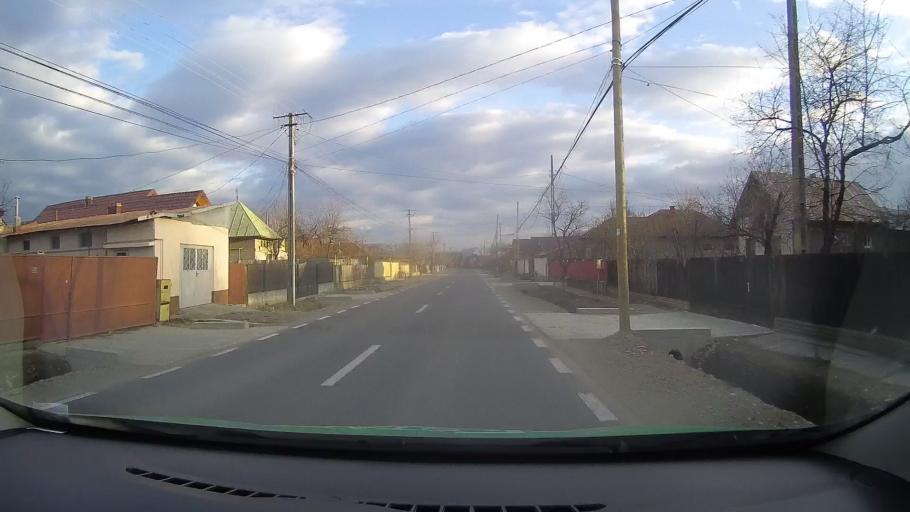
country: RO
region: Dambovita
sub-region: Comuna I. L. Caragiale
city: Ghirdoveni
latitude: 44.9490
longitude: 25.6588
